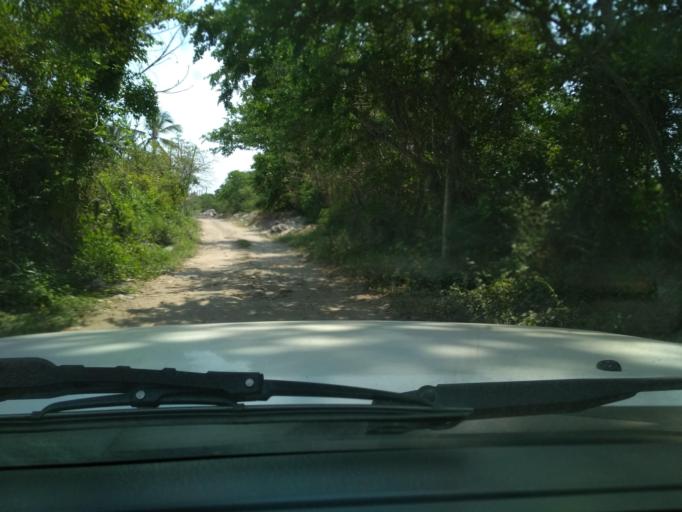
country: MX
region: Veracruz
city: Boca del Rio
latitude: 19.1086
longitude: -96.1266
